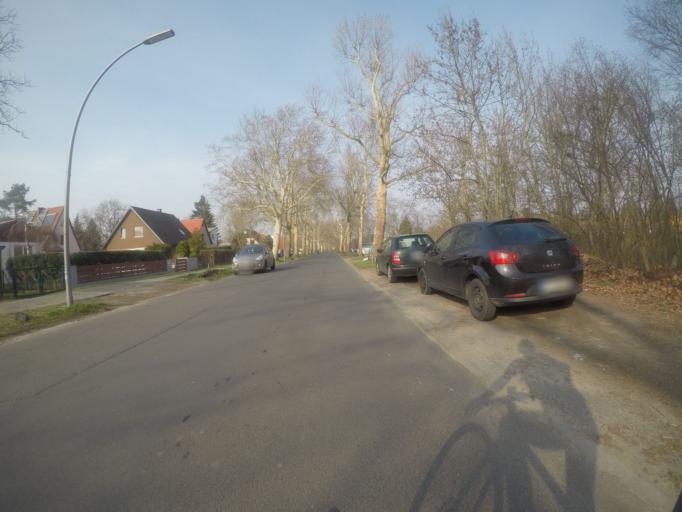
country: DE
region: Berlin
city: Rudow
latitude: 52.4069
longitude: 13.4917
